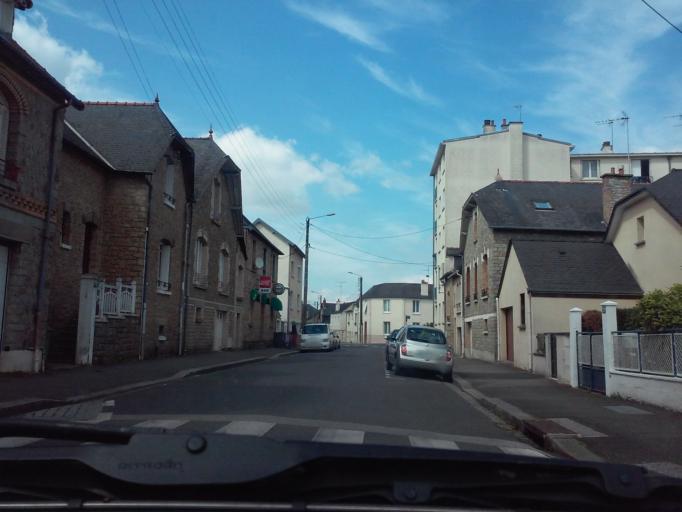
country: FR
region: Brittany
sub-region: Departement d'Ille-et-Vilaine
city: Rennes
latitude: 48.0966
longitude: -1.6672
